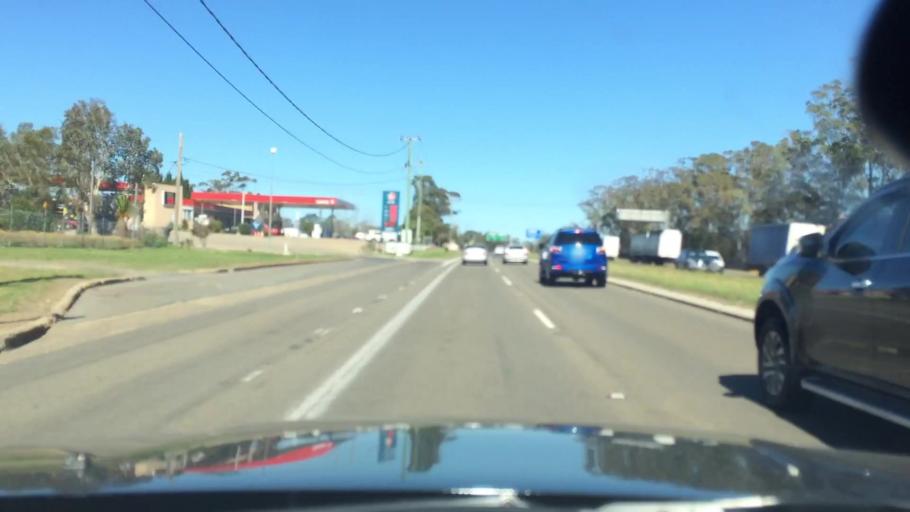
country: AU
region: New South Wales
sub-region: Campbelltown Municipality
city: Glenfield
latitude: -33.9623
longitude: 150.8817
